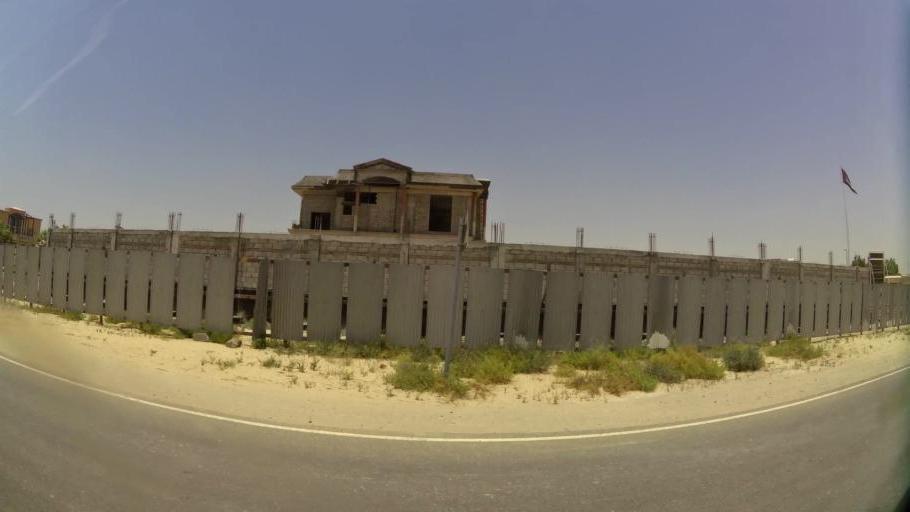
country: AE
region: Ajman
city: Ajman
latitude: 25.4123
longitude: 55.4943
